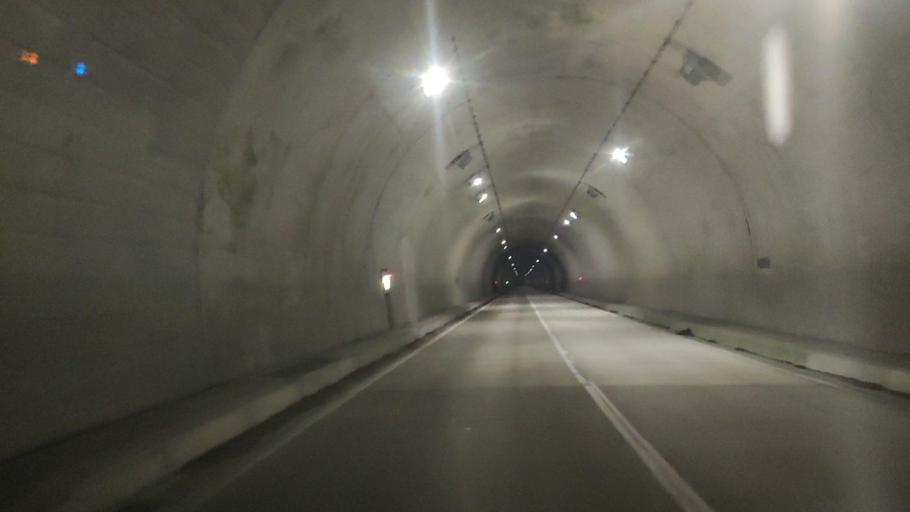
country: JP
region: Kumamoto
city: Matsubase
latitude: 32.4780
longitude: 130.8863
